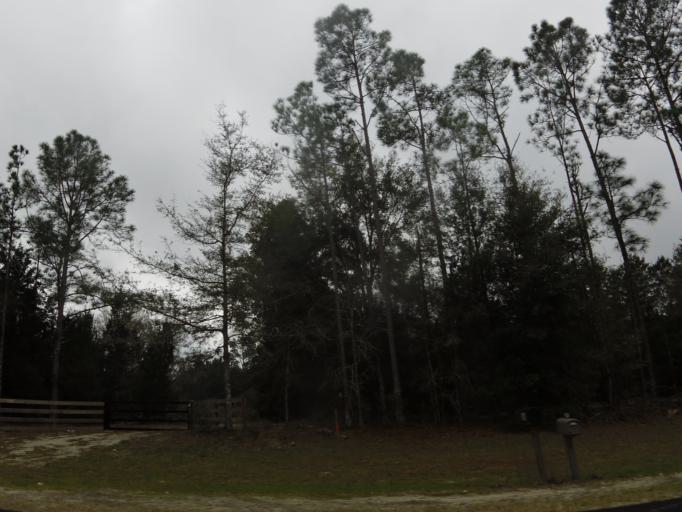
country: US
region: Florida
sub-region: Alachua County
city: High Springs
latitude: 29.8145
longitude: -82.7189
